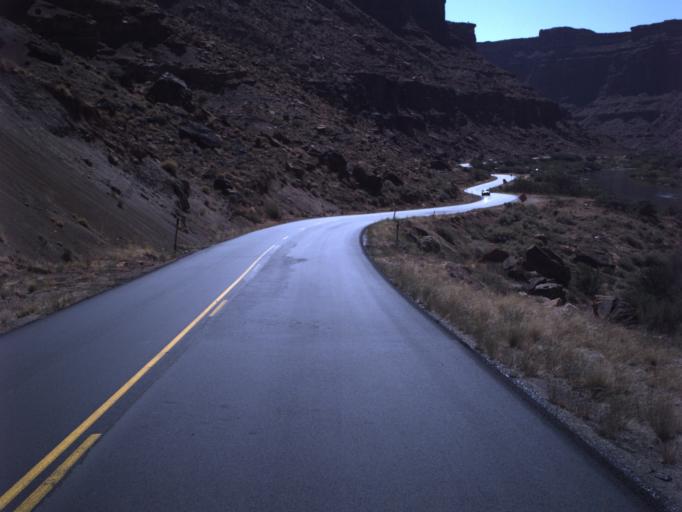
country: US
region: Utah
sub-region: Grand County
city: Moab
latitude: 38.6676
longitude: -109.4986
